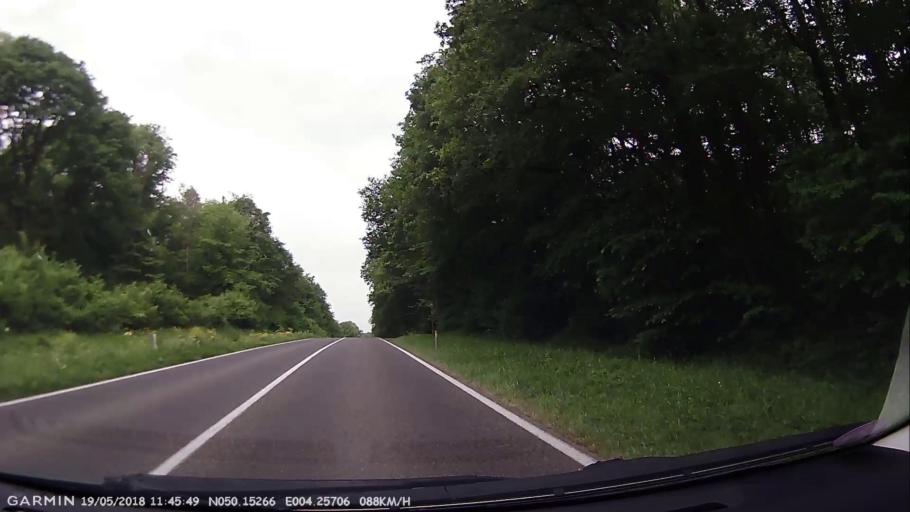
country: BE
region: Wallonia
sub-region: Province du Hainaut
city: Froidchapelle
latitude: 50.1530
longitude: 4.2566
